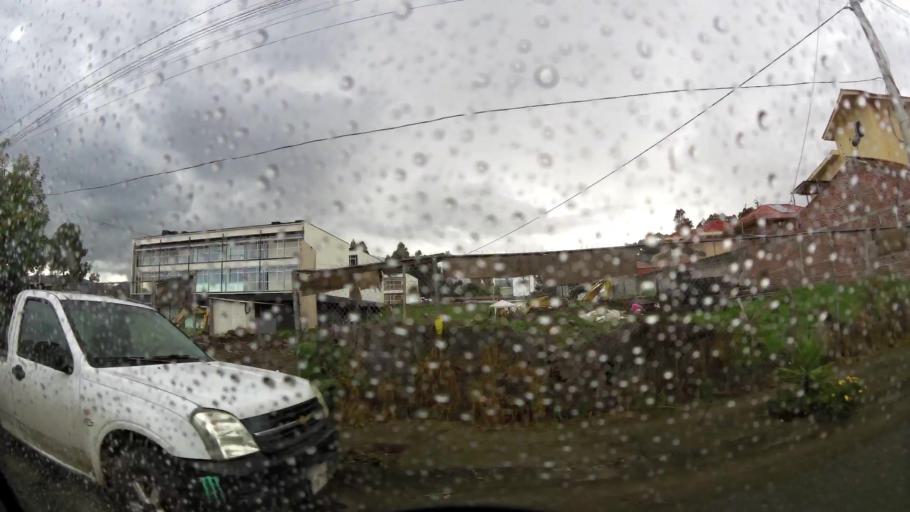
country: EC
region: Azuay
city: Cuenca
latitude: -2.8922
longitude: -79.0349
